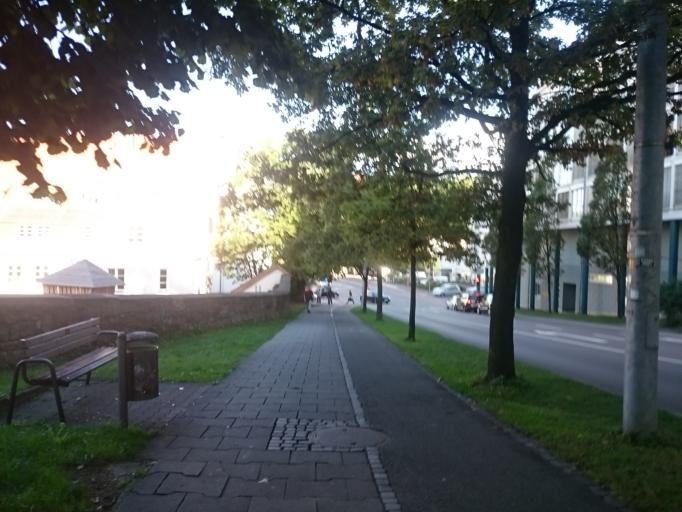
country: DE
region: Bavaria
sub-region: Swabia
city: Kempten (Allgaeu)
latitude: 47.7242
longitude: 10.3168
